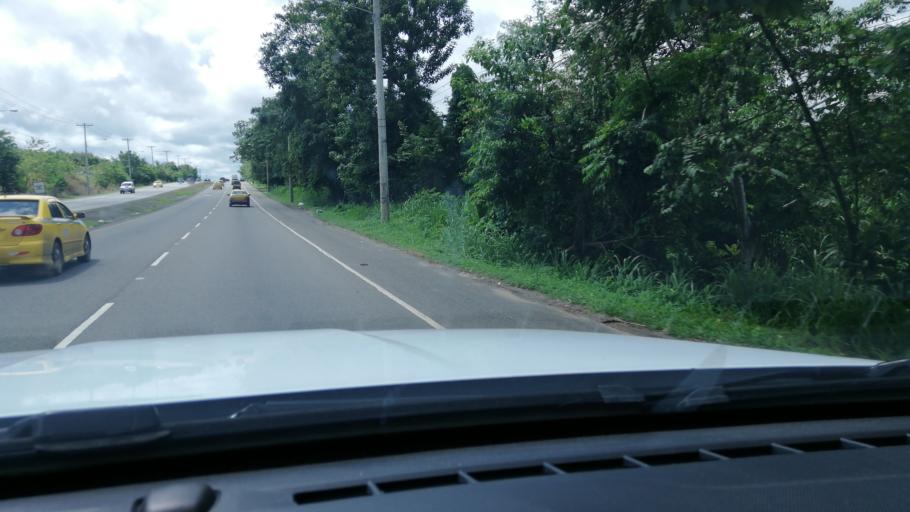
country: PA
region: Panama
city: Cabra Numero Uno
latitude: 9.1009
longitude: -79.3352
